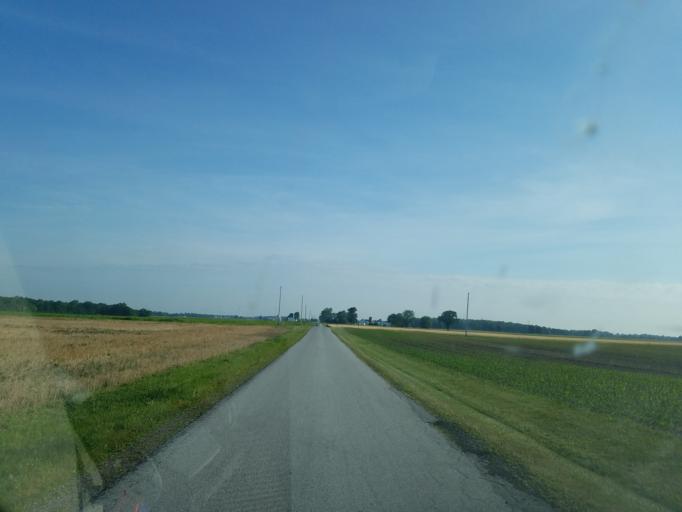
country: US
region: Ohio
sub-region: Hardin County
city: Kenton
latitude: 40.7600
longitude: -83.6716
